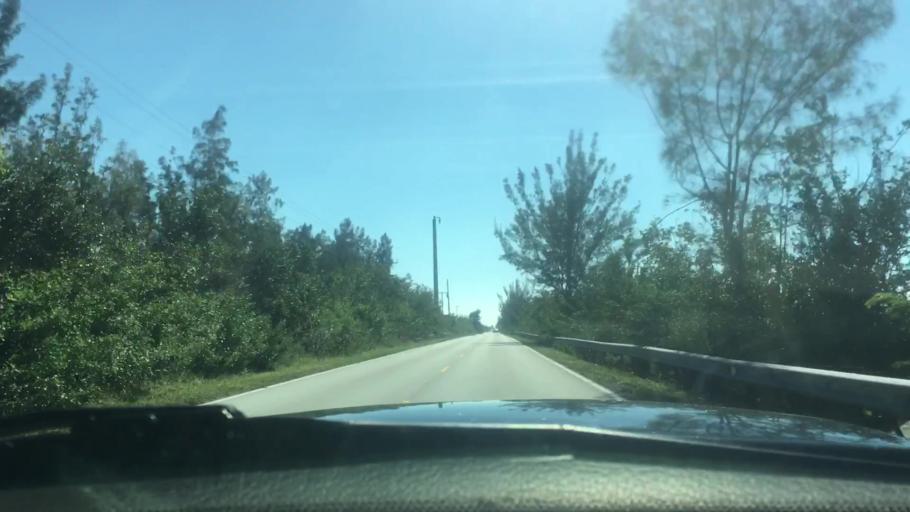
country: US
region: Florida
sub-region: Miami-Dade County
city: Florida City
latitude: 25.3649
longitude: -80.4286
